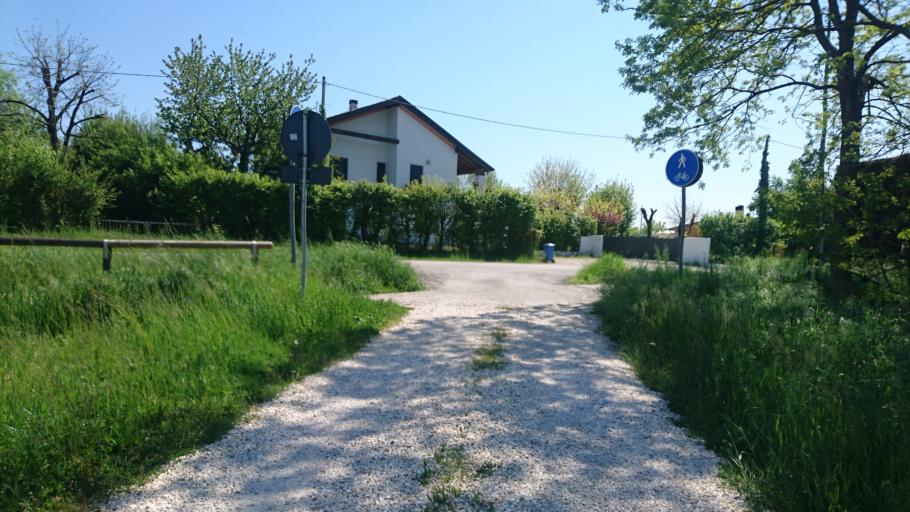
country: IT
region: Veneto
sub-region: Provincia di Treviso
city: Conscio
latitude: 45.6330
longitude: 12.2745
